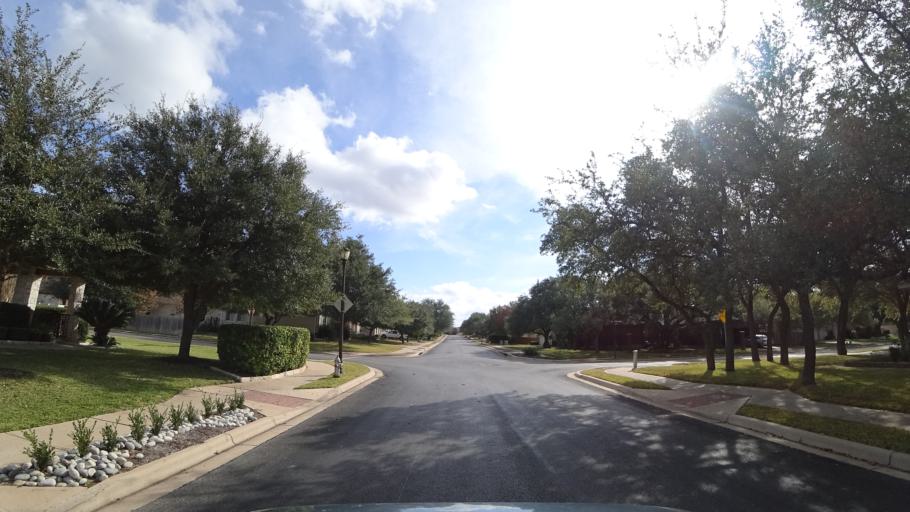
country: US
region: Texas
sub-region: Williamson County
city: Brushy Creek
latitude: 30.5132
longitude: -97.7476
